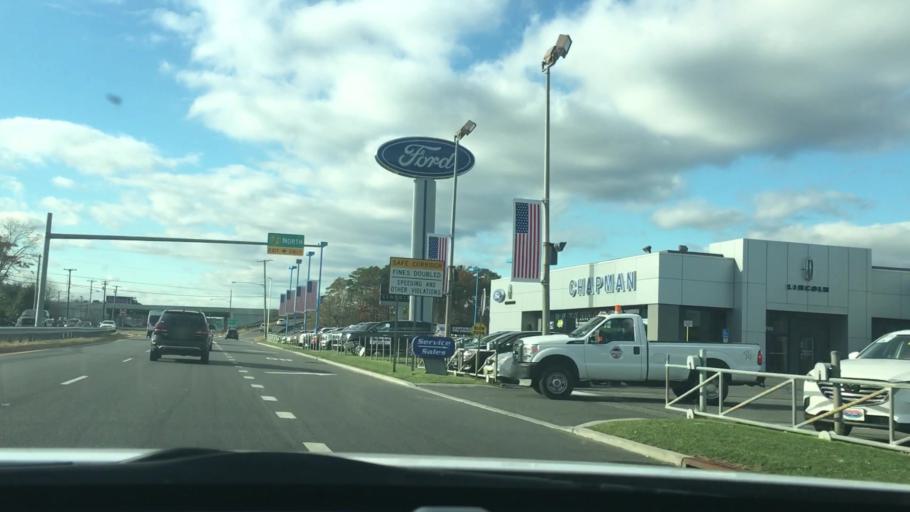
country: US
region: New Jersey
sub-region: Atlantic County
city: Northfield
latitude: 39.3992
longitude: -74.5564
